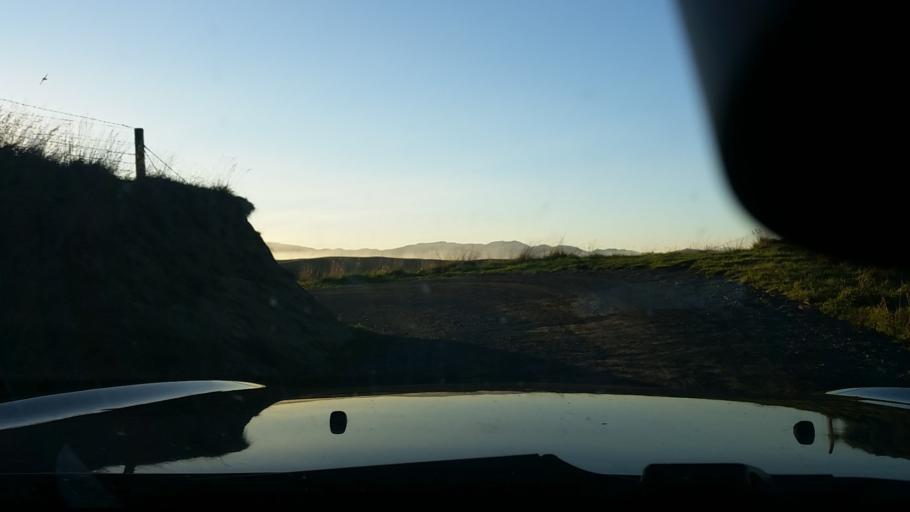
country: NZ
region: Marlborough
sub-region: Marlborough District
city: Blenheim
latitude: -41.7483
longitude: 174.0582
